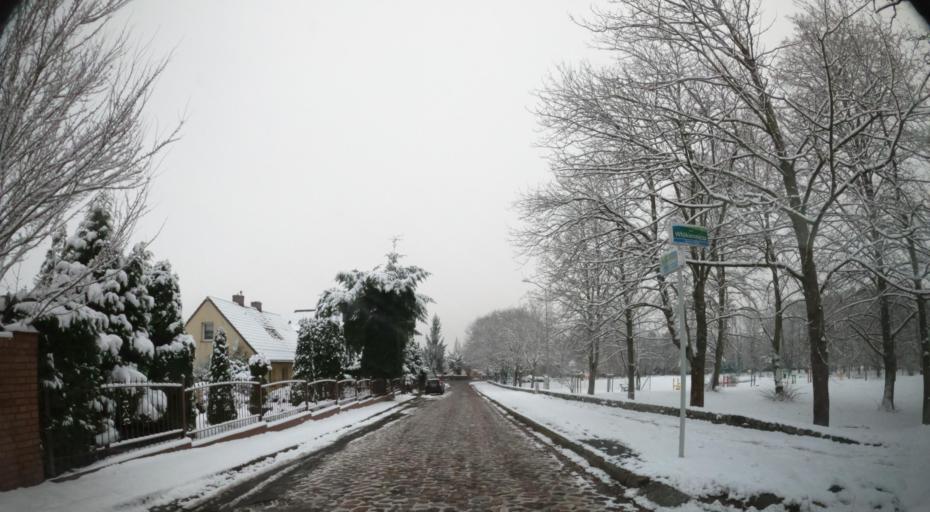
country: PL
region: West Pomeranian Voivodeship
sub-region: Szczecin
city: Szczecin
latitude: 53.3529
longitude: 14.5797
